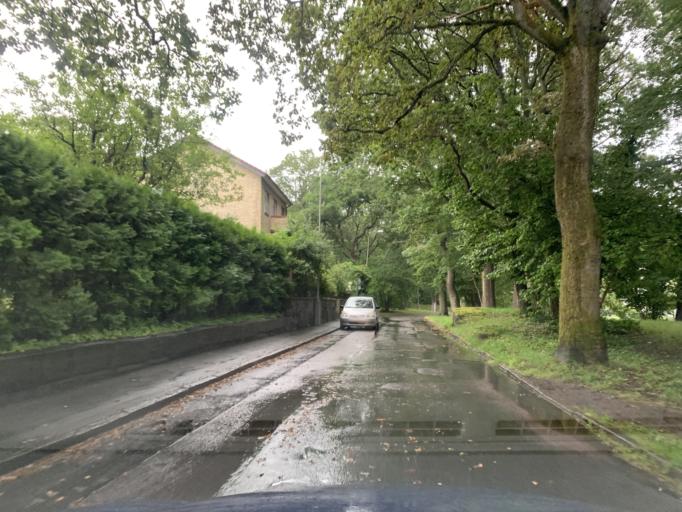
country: SE
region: Vaestra Goetaland
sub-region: Molndal
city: Moelndal
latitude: 57.7054
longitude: 12.0171
